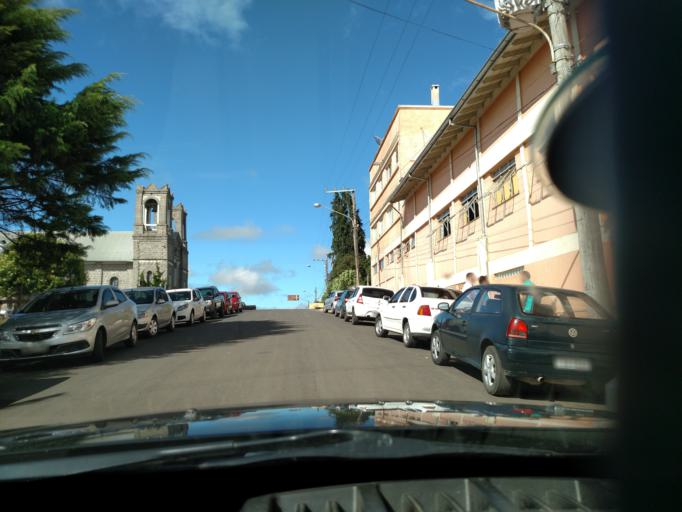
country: BR
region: Santa Catarina
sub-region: Sao Joaquim
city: Sao Joaquim
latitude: -28.2935
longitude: -49.9317
